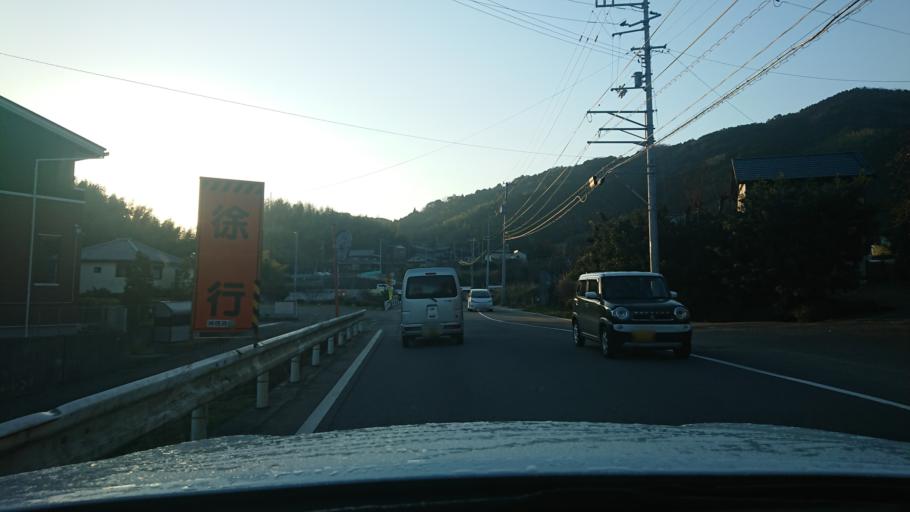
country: JP
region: Tokushima
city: Komatsushimacho
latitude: 33.9496
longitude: 134.5616
